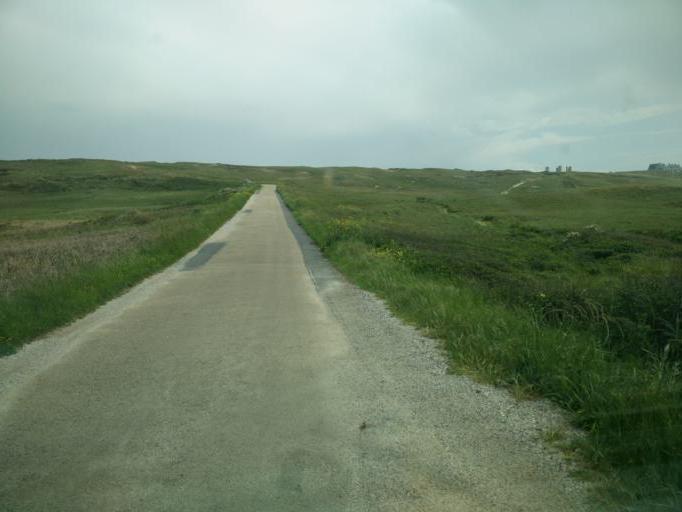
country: FR
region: Brittany
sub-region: Departement du Finistere
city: Camaret-sur-Mer
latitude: 48.2790
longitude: -4.6156
